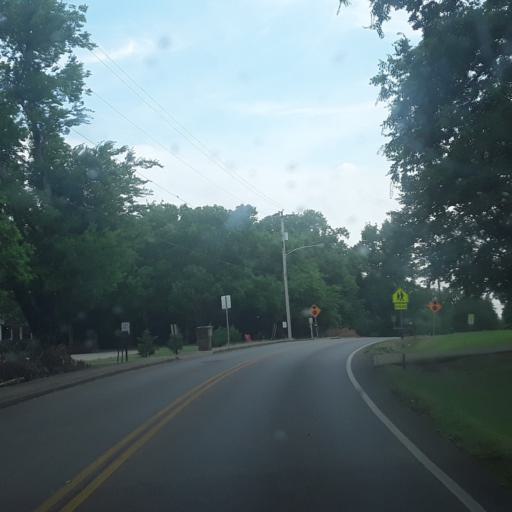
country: US
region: Tennessee
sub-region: Williamson County
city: Brentwood
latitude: 36.0598
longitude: -86.7224
